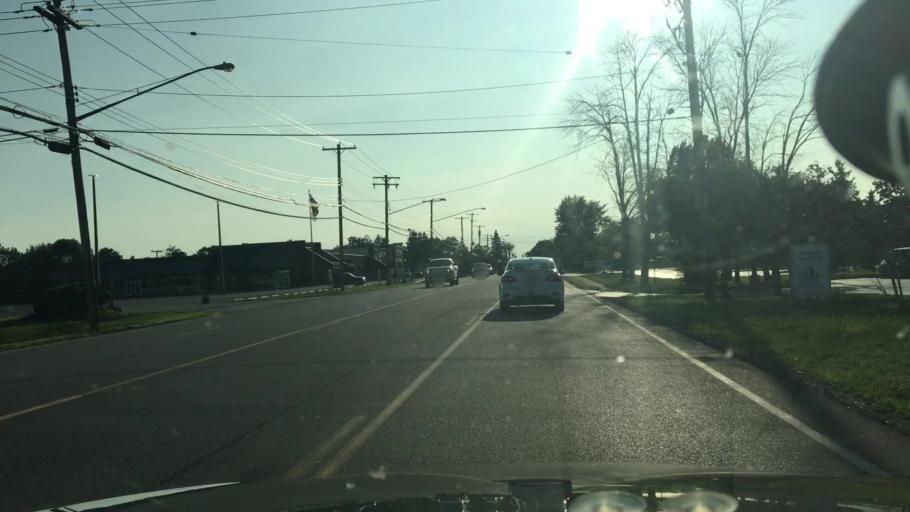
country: US
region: New York
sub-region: Erie County
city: Blasdell
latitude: 42.7971
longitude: -78.8204
